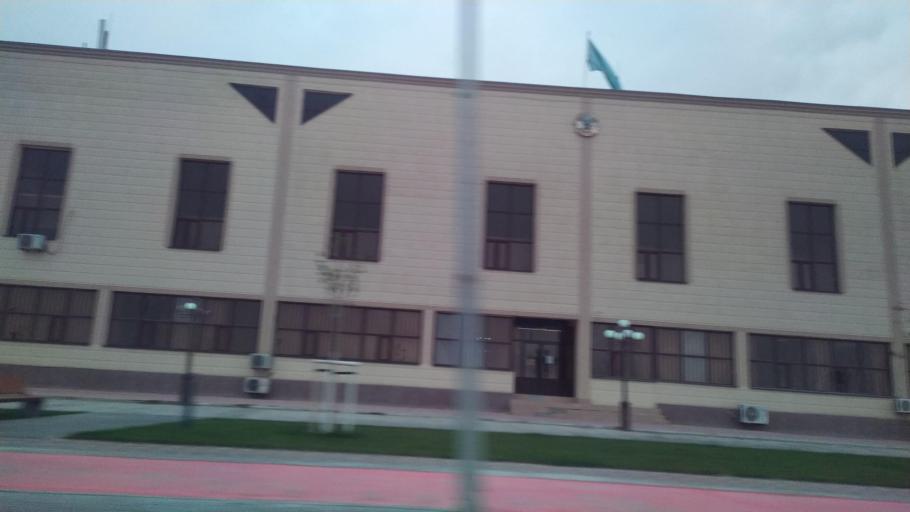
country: KZ
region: Ongtustik Qazaqstan
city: Turkestan
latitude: 43.2806
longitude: 68.3206
